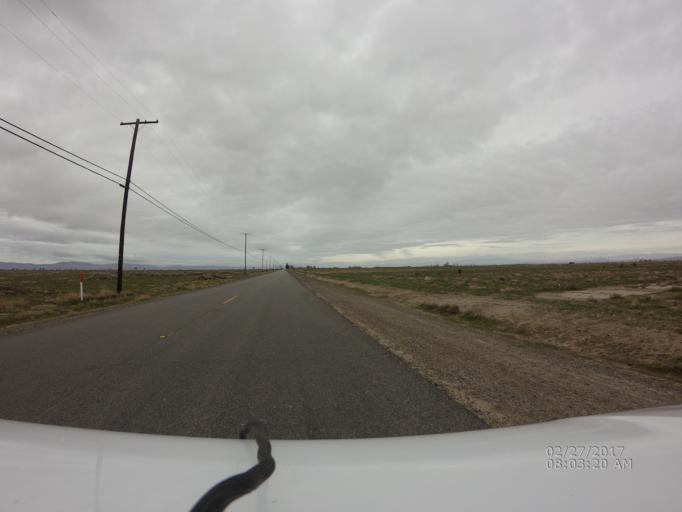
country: US
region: California
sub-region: Los Angeles County
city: Lancaster
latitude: 34.7049
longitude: -117.9787
